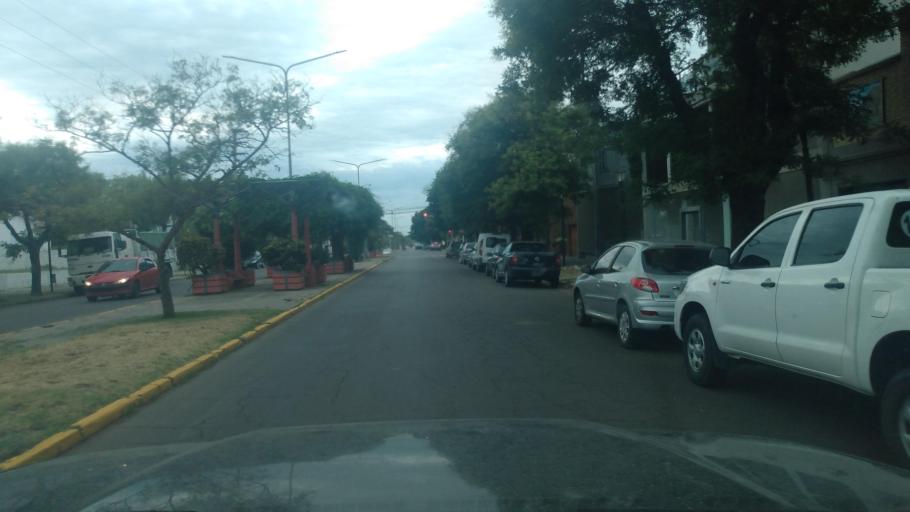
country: AR
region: Buenos Aires
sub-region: Partido de Trenque Lauquen
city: Trenque Lauquen
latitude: -35.9774
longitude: -62.7304
